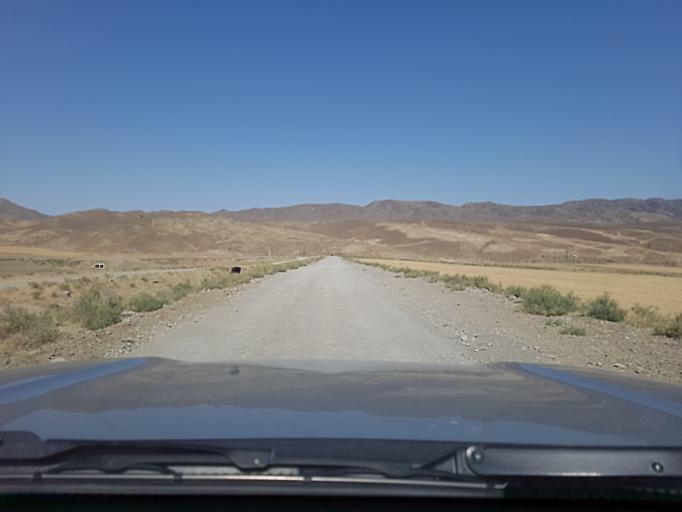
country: TM
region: Ahal
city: Baharly
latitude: 38.4124
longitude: 57.0205
